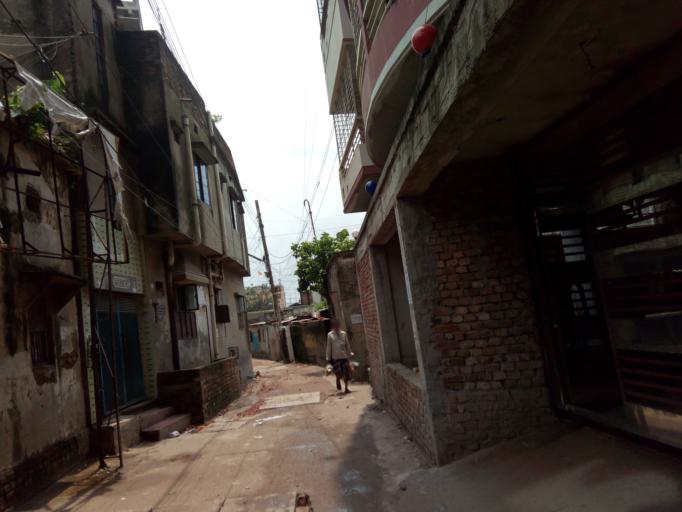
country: BD
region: Dhaka
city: Azimpur
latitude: 23.7484
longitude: 90.3632
